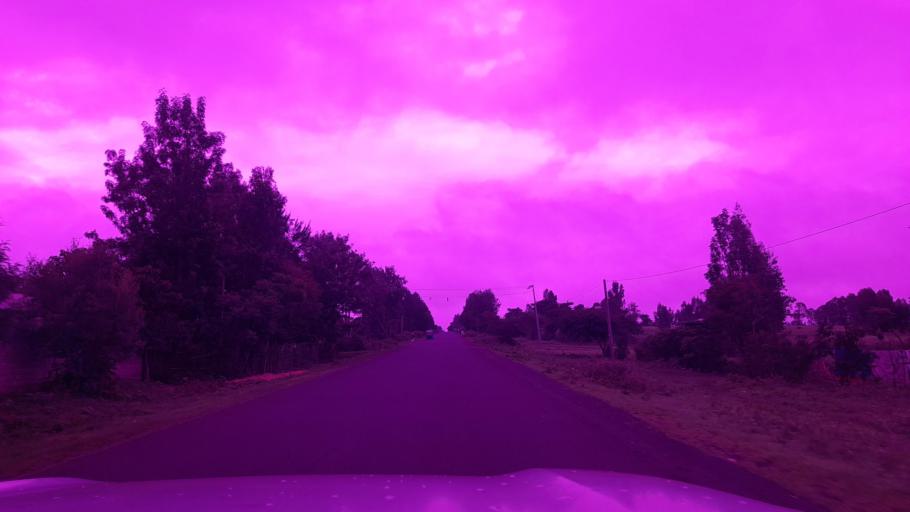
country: ET
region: Oromiya
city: Waliso
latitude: 8.2666
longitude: 37.6562
